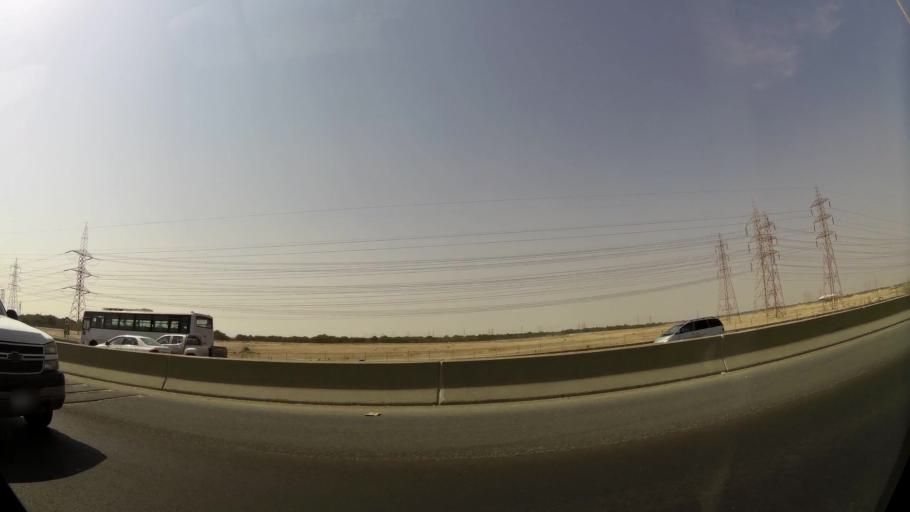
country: KW
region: Al Ahmadi
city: Al Fahahil
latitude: 29.0514
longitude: 48.1116
